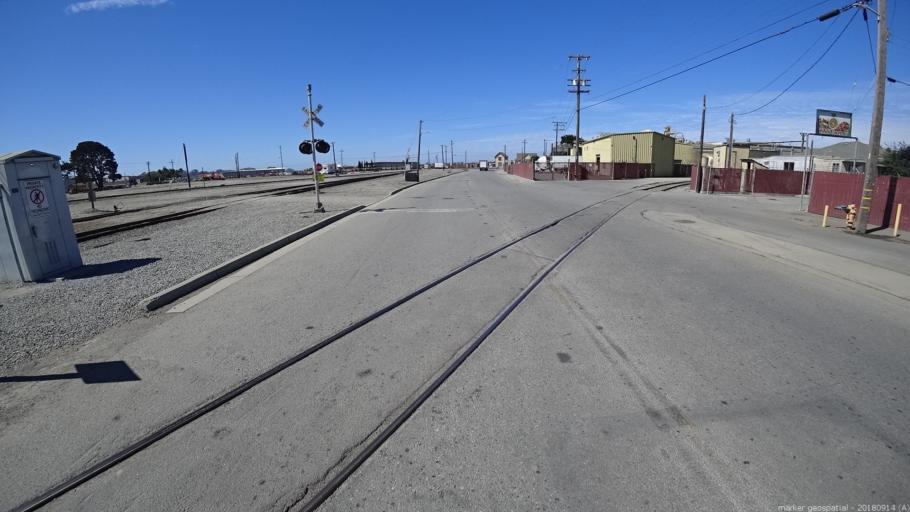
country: US
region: California
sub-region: Monterey County
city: Pajaro
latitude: 36.8959
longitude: -121.7459
